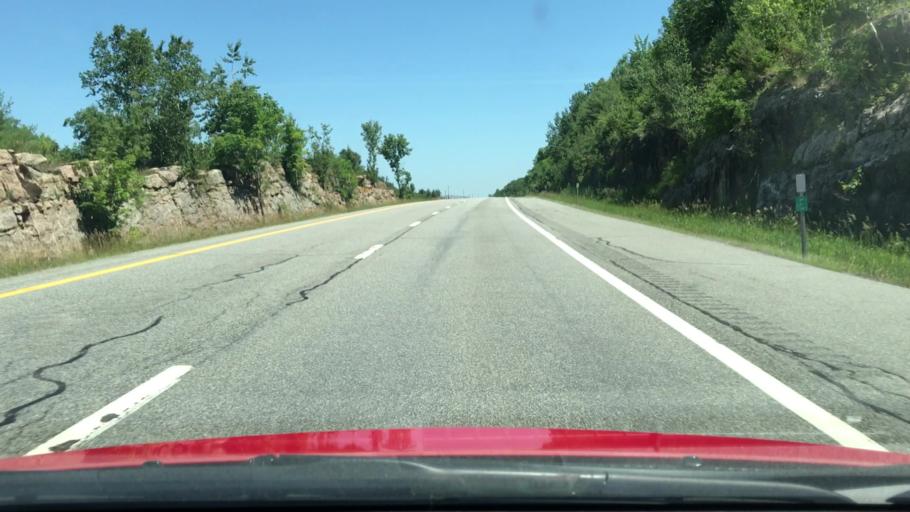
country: US
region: New York
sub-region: Essex County
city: Elizabethtown
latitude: 44.1793
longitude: -73.5765
